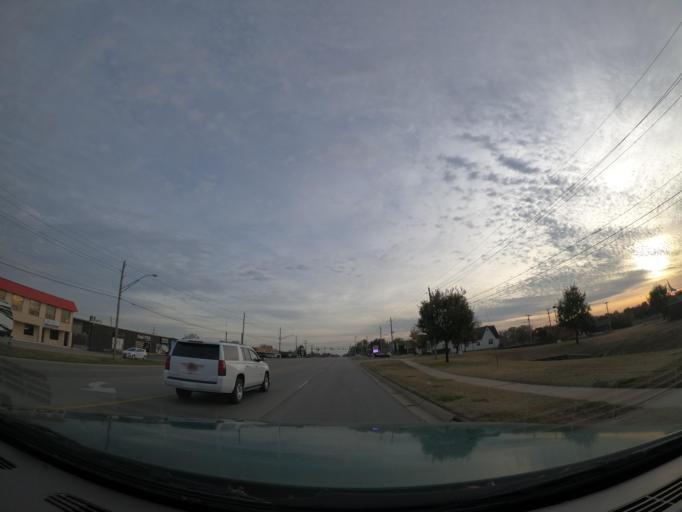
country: US
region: Oklahoma
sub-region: Tulsa County
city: Broken Arrow
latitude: 36.0562
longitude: -95.8154
